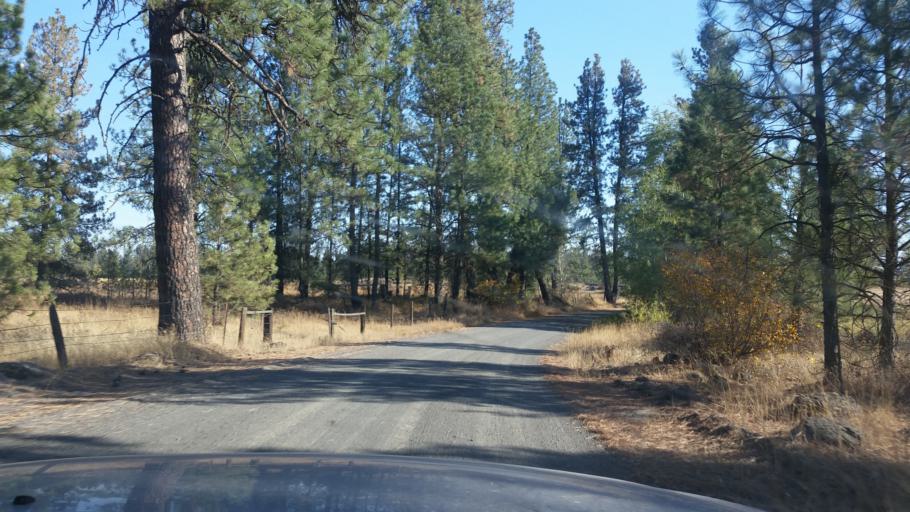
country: US
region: Washington
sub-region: Spokane County
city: Cheney
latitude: 47.4291
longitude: -117.6533
